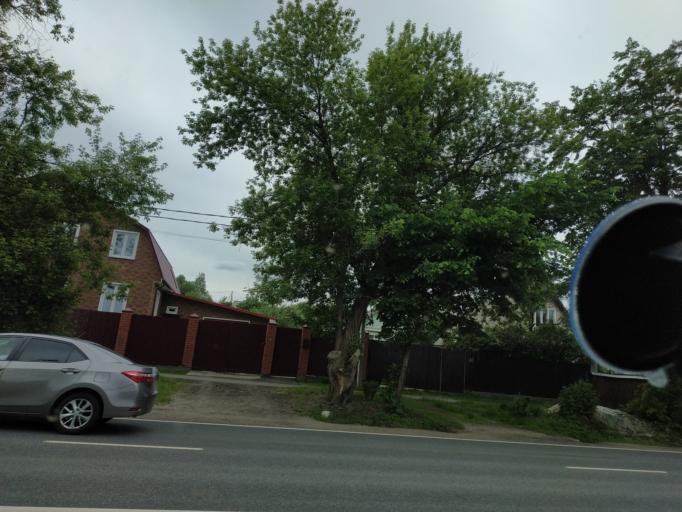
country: RU
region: Moskovskaya
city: Ostrovtsy
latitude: 55.5567
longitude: 38.0559
